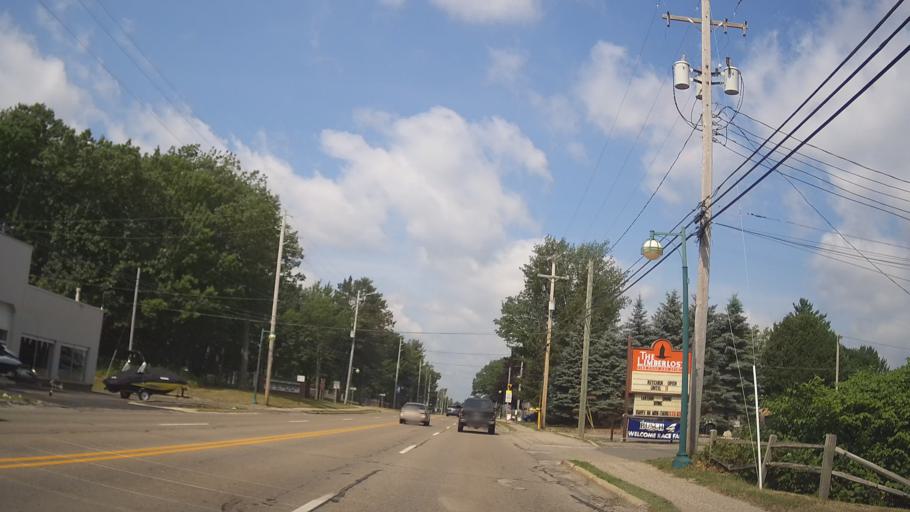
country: US
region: Michigan
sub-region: Roscommon County
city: Houghton Lake
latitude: 44.2985
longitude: -84.7219
